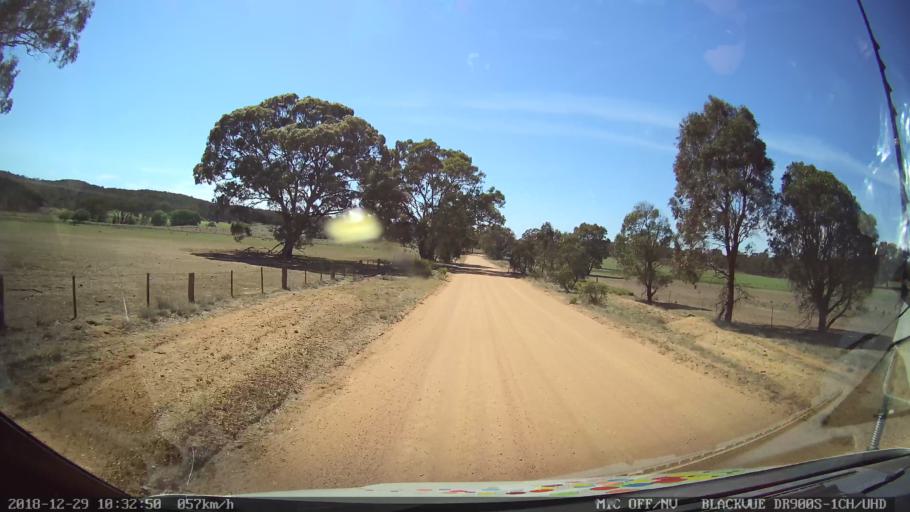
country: AU
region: New South Wales
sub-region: Yass Valley
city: Gundaroo
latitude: -34.9766
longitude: 149.4683
